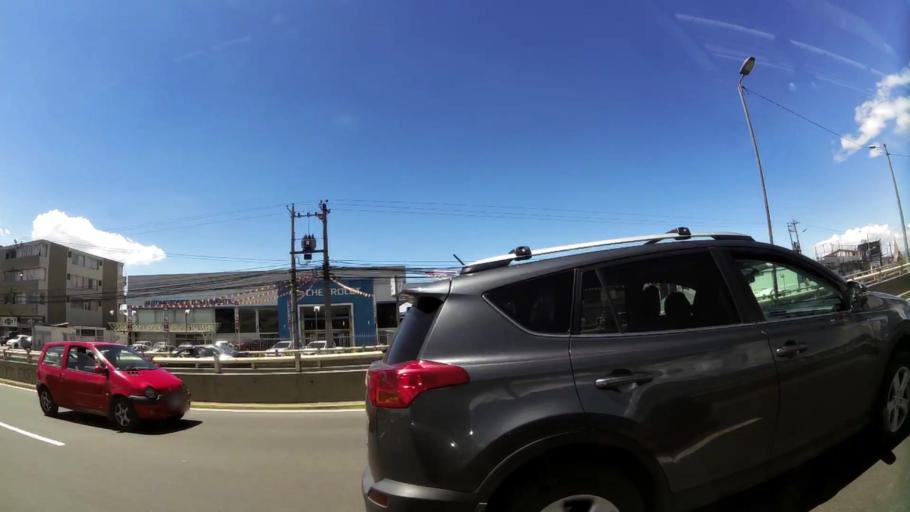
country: EC
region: Pichincha
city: Quito
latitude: -0.1562
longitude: -78.4850
